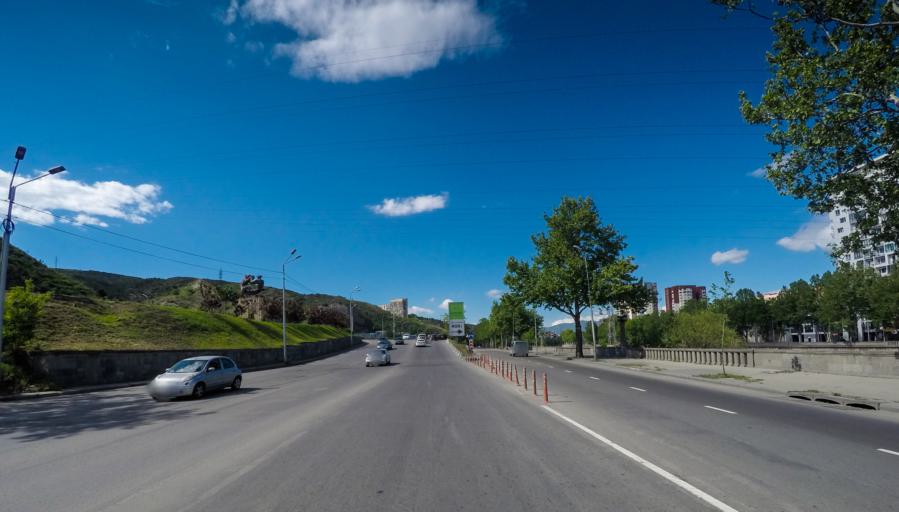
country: GE
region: T'bilisi
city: Tbilisi
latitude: 41.7394
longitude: 44.7708
